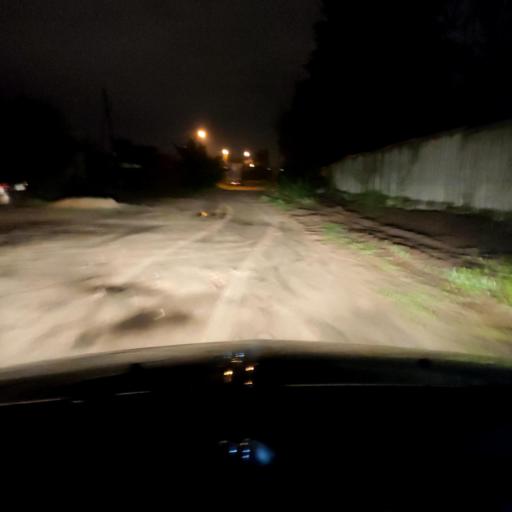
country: RU
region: Voronezj
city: Maslovka
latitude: 51.6054
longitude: 39.2247
